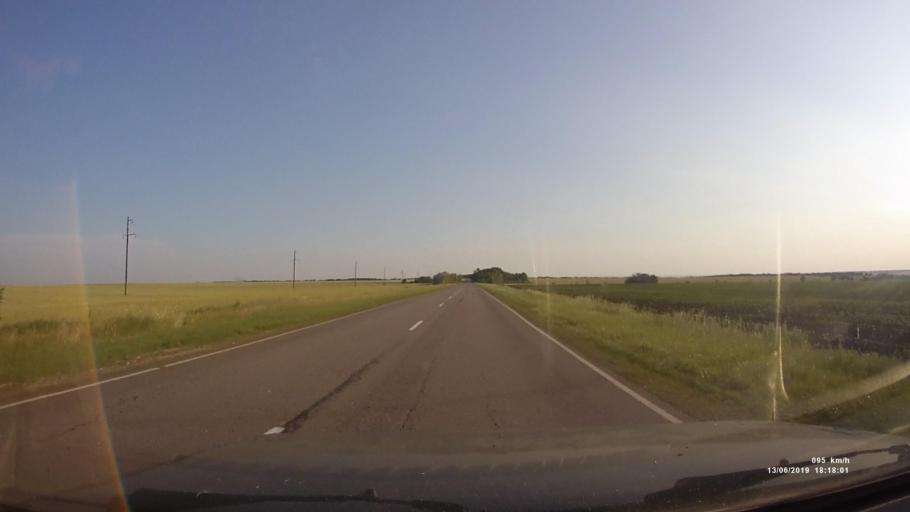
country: RU
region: Rostov
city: Kazanskaya
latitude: 49.9130
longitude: 41.3189
